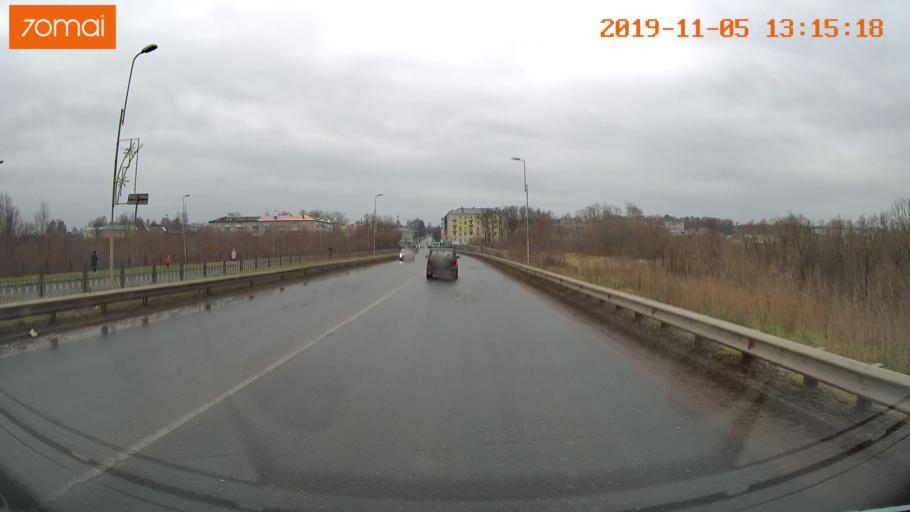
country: RU
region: Ivanovo
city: Shuya
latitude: 56.8508
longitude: 41.3628
